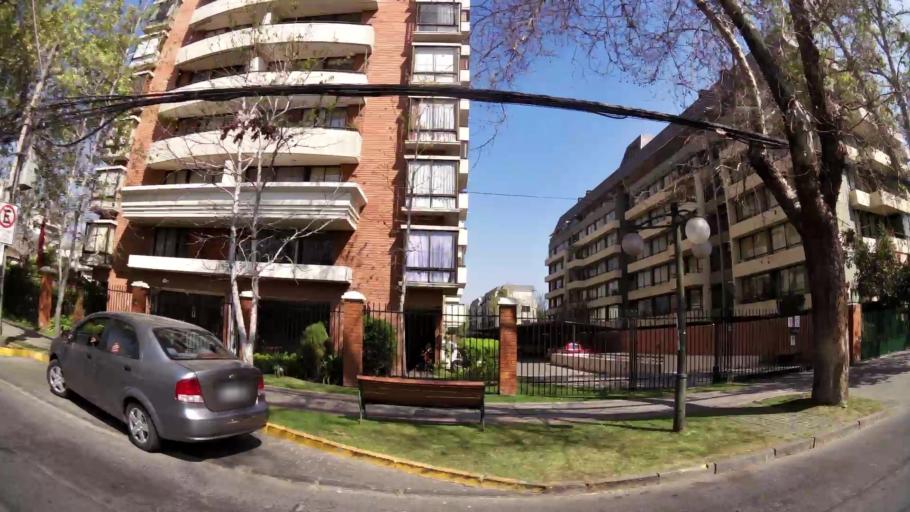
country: CL
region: Santiago Metropolitan
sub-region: Provincia de Santiago
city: Santiago
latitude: -33.4557
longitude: -70.6200
